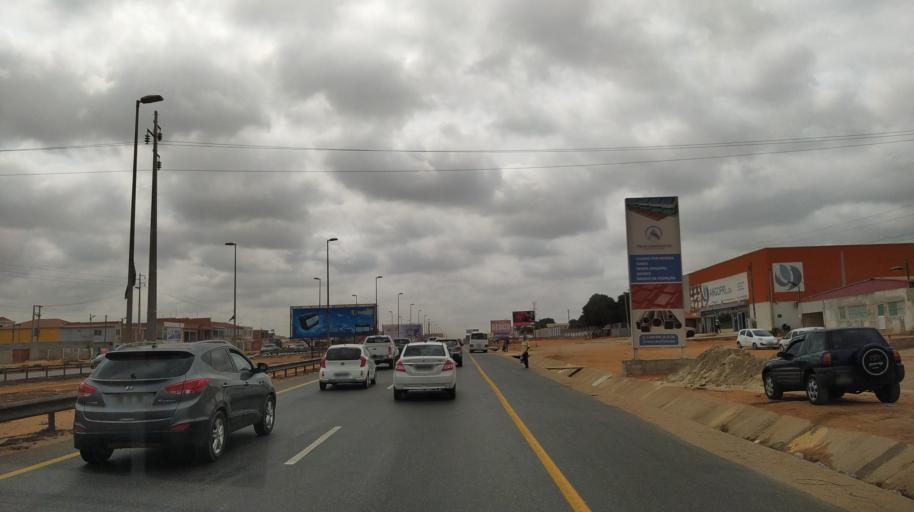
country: AO
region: Luanda
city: Luanda
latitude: -8.9730
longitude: 13.3084
